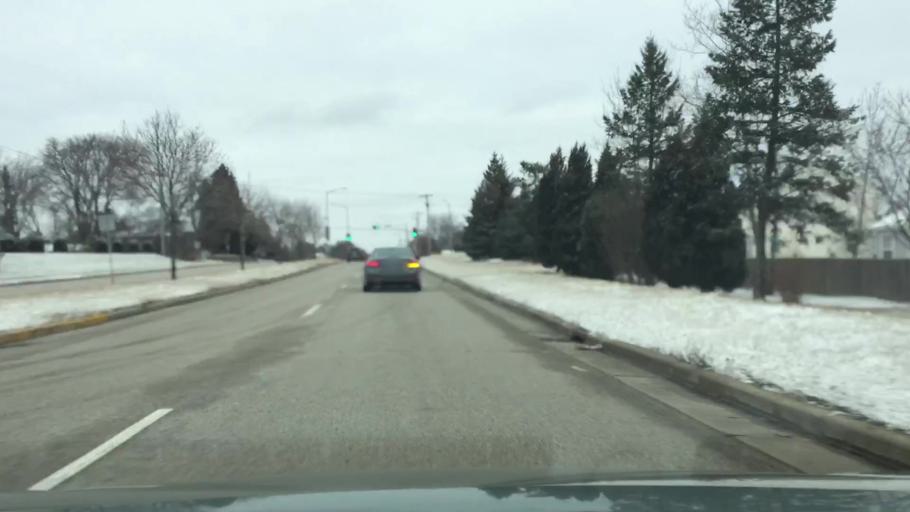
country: US
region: Wisconsin
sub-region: Waukesha County
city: Butler
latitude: 43.1325
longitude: -88.1047
